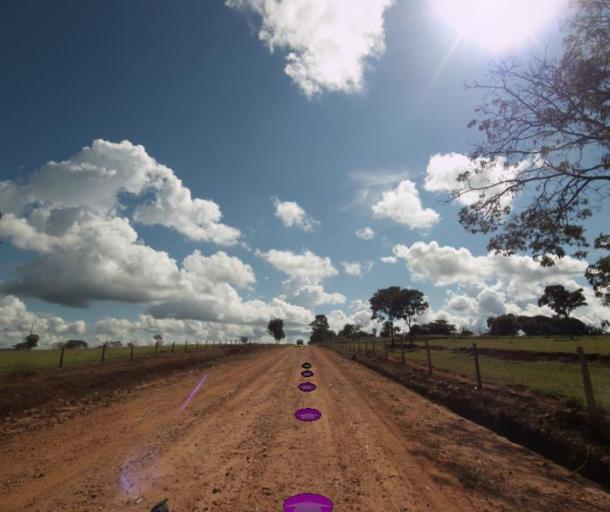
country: BR
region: Goias
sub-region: Pirenopolis
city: Pirenopolis
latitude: -15.8287
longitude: -49.1332
